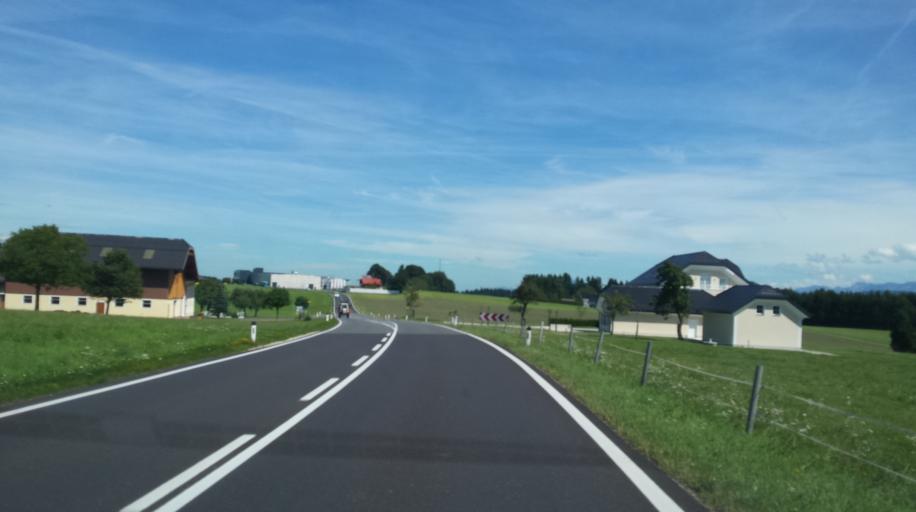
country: AT
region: Upper Austria
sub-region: Politischer Bezirk Vocklabruck
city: Oberhofen am Irrsee
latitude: 47.9926
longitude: 13.3144
